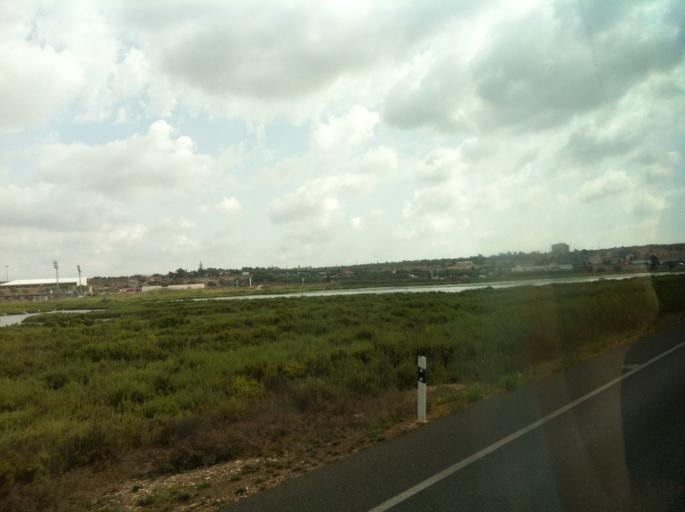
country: ES
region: Valencia
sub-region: Provincia de Alicante
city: Santa Pola
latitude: 38.1973
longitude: -0.5755
